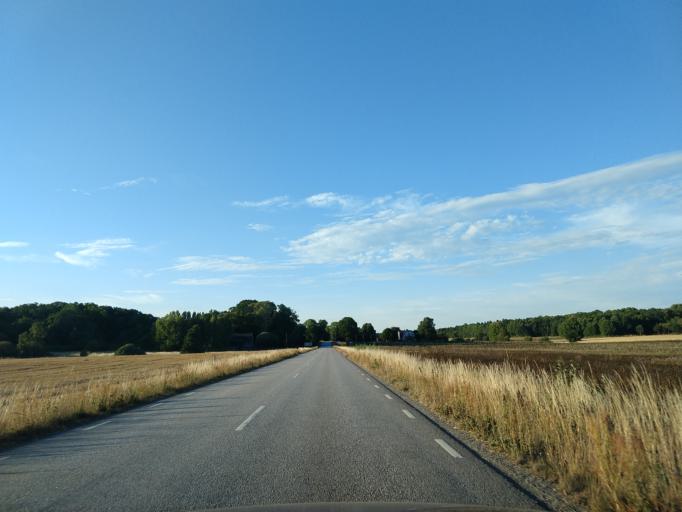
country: SE
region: Blekinge
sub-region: Ronneby Kommun
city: Brakne-Hoby
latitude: 56.2493
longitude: 15.1155
